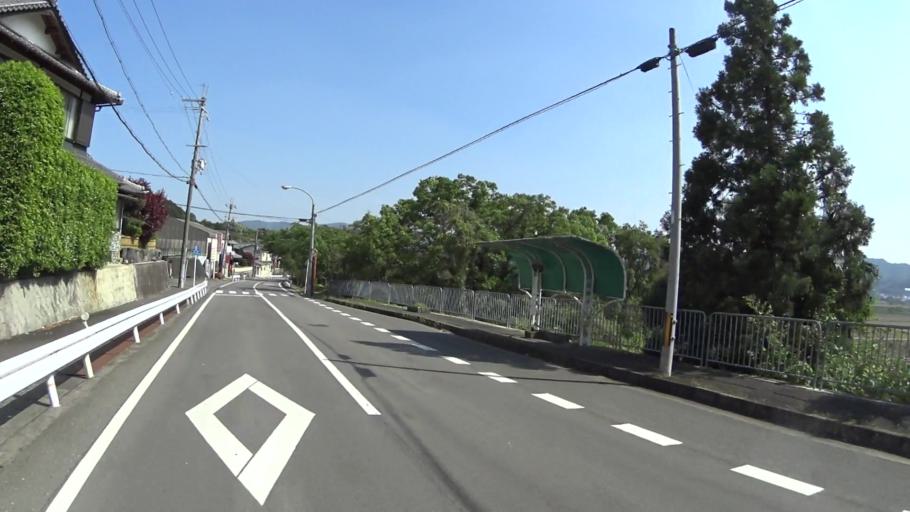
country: JP
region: Kyoto
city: Kameoka
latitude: 35.0323
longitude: 135.5878
